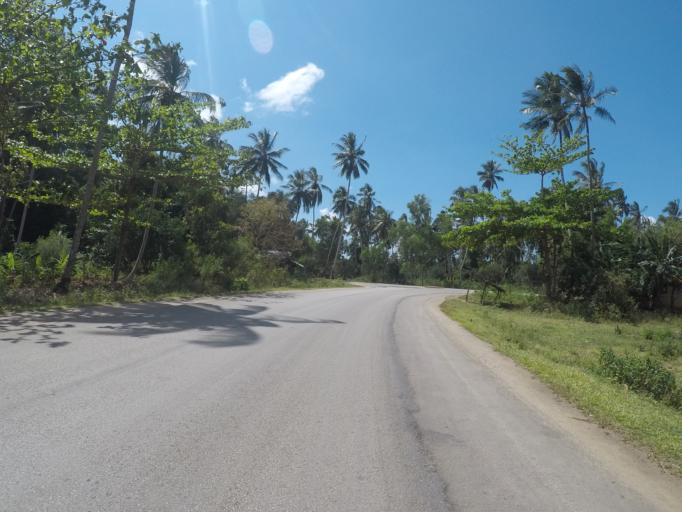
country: TZ
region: Zanzibar Central/South
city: Koani
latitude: -6.1416
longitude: 39.3271
